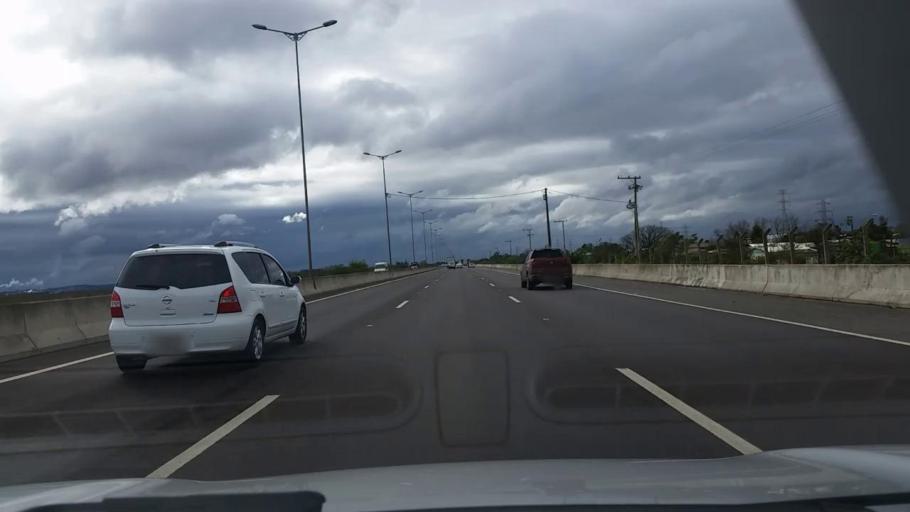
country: BR
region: Rio Grande do Sul
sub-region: Canoas
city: Canoas
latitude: -29.9529
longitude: -51.2029
